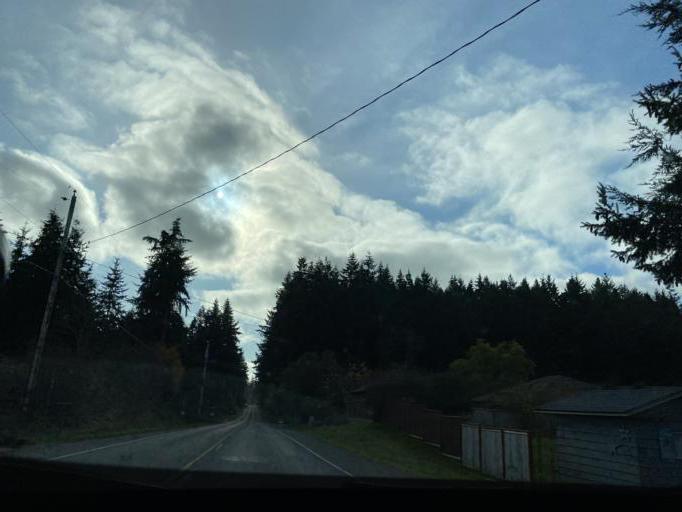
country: US
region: Washington
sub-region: Island County
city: Freeland
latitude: 47.9860
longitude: -122.4618
